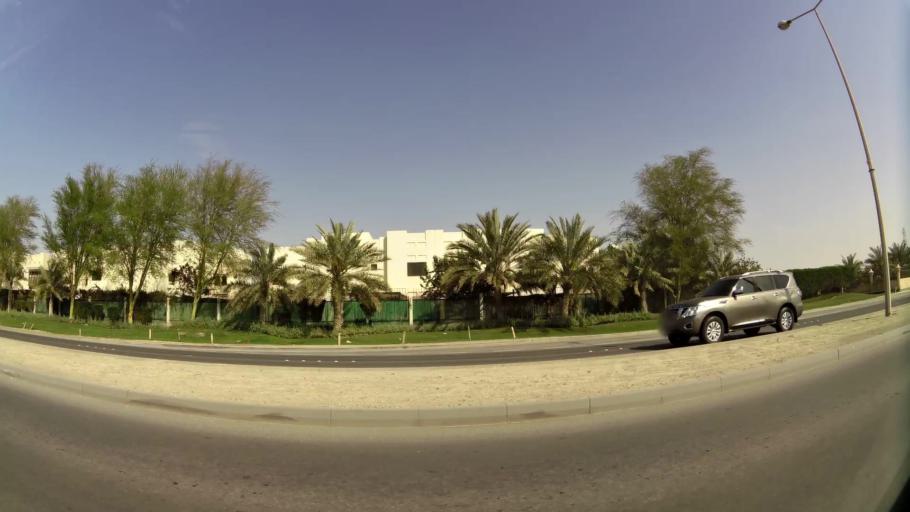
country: BH
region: Central Governorate
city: Madinat Hamad
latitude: 26.1782
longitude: 50.4656
